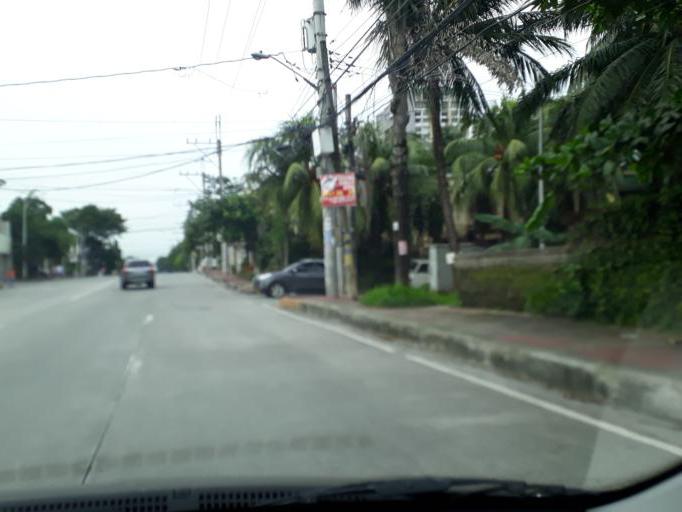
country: PH
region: Calabarzon
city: Del Monte
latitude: 14.6318
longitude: 121.0302
